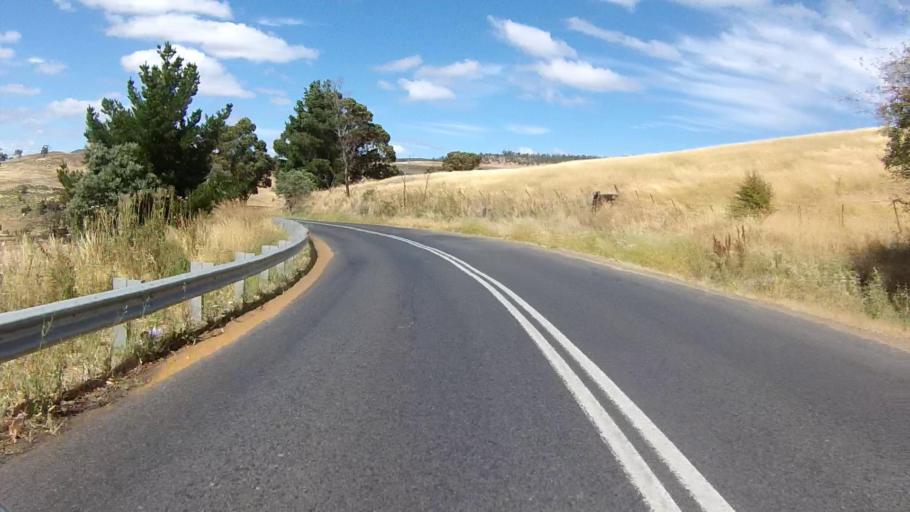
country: AU
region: Tasmania
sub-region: Brighton
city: Bridgewater
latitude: -42.5659
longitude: 147.3905
